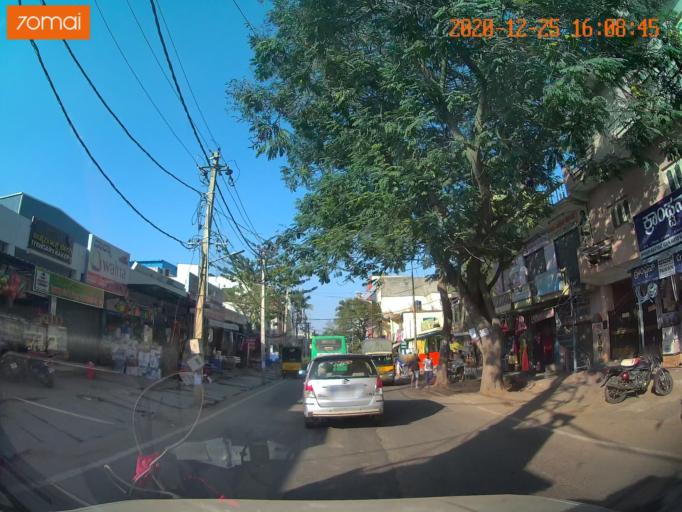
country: IN
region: Karnataka
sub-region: Bangalore Urban
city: Bangalore
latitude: 12.8979
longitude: 77.6264
